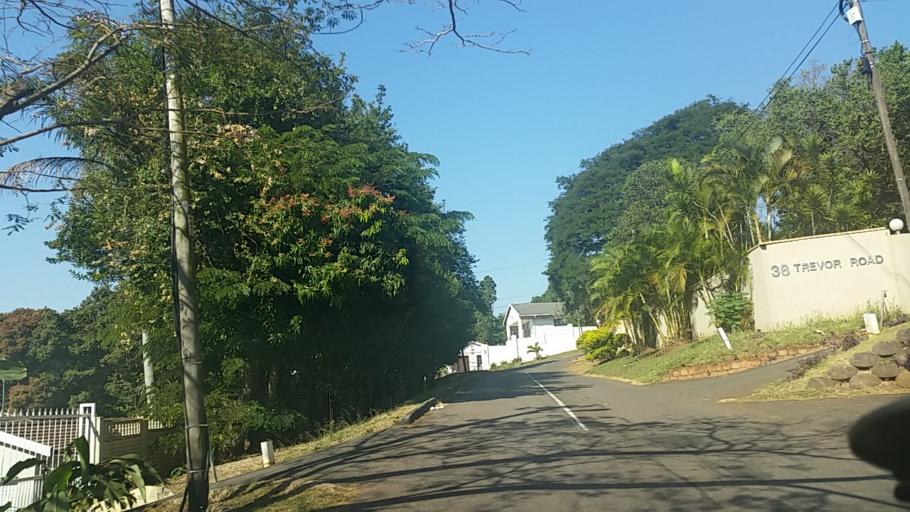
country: ZA
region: KwaZulu-Natal
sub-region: eThekwini Metropolitan Municipality
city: Berea
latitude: -29.8522
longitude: 30.9032
